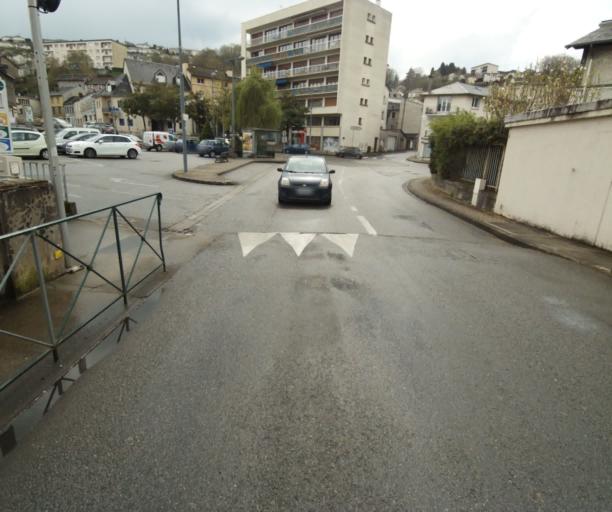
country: FR
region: Limousin
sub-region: Departement de la Correze
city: Tulle
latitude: 45.2599
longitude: 1.7527
